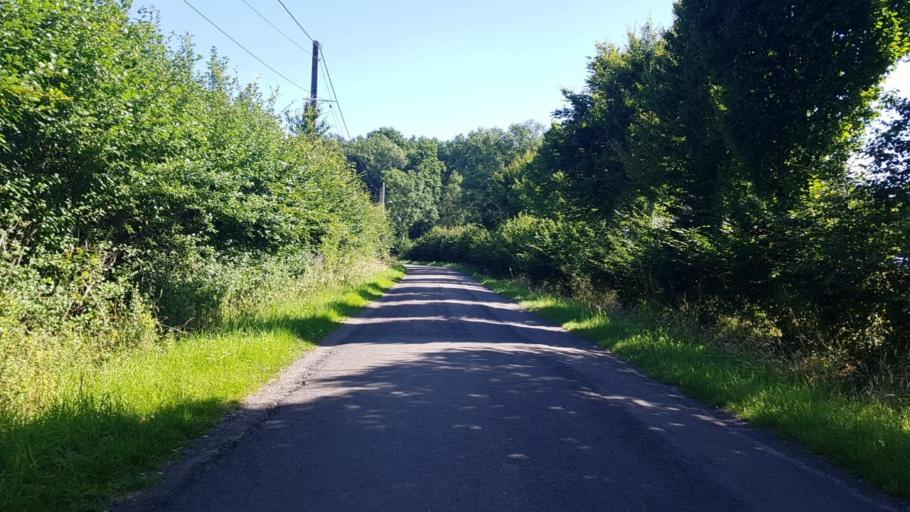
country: FR
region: Nord-Pas-de-Calais
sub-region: Departement du Nord
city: Anor
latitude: 49.9808
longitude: 4.1289
